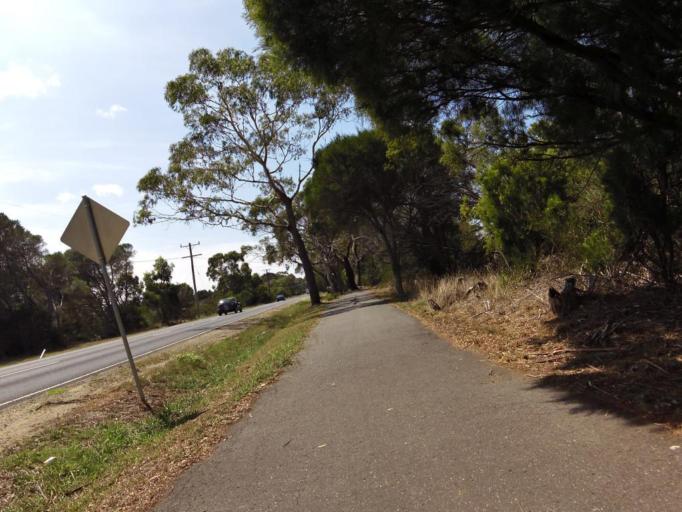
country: AU
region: Victoria
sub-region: Mornington Peninsula
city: Crib Point
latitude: -38.3344
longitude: 145.1795
